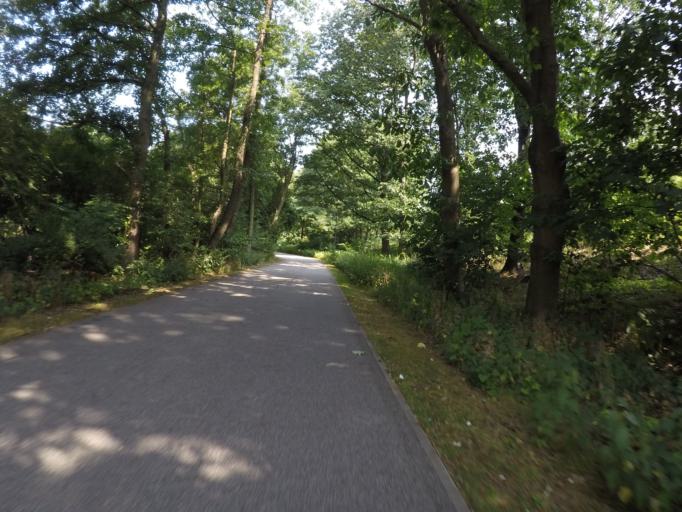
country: DE
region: Hamburg
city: Kleiner Grasbrook
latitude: 53.5049
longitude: 9.9981
